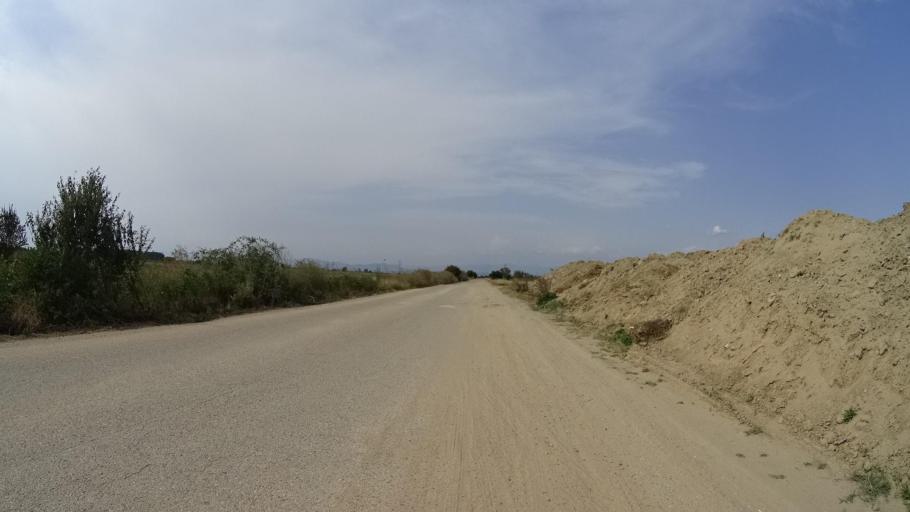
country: BG
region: Plovdiv
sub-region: Obshtina Kaloyanovo
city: Kaloyanovo
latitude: 42.3128
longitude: 24.7996
